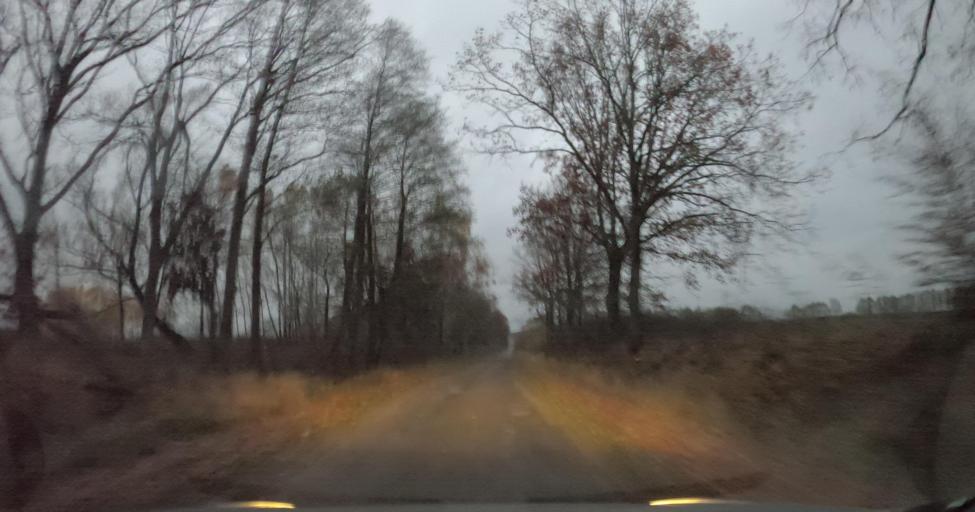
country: PL
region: West Pomeranian Voivodeship
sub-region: Powiat bialogardzki
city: Tychowo
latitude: 53.8526
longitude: 16.2402
